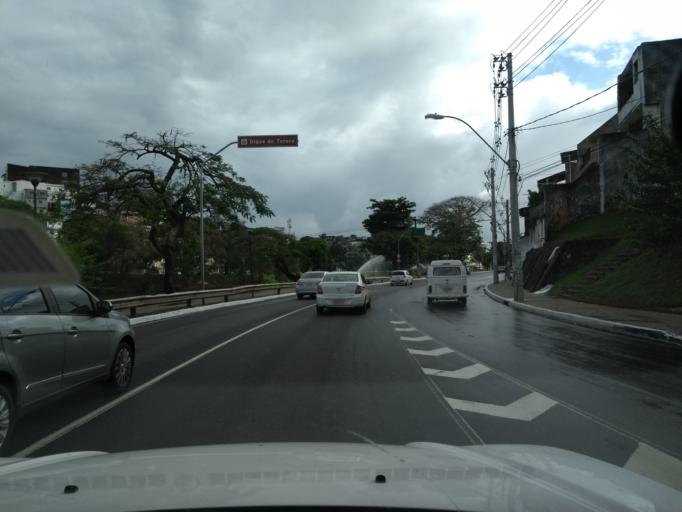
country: BR
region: Bahia
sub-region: Salvador
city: Salvador
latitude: -12.9873
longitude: -38.5078
